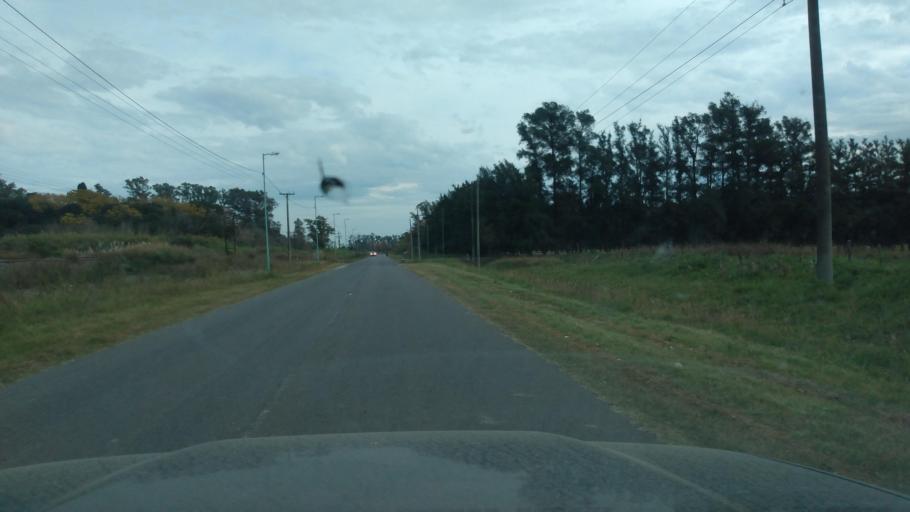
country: AR
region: Buenos Aires
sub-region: Partido de Lujan
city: Lujan
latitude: -34.5944
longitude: -59.1535
